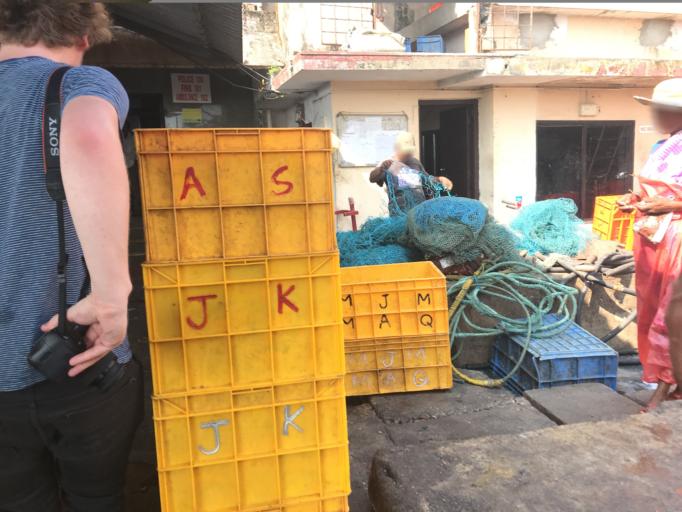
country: IN
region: Karnataka
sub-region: Dakshina Kannada
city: Ullal
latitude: 12.8553
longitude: 74.8332
